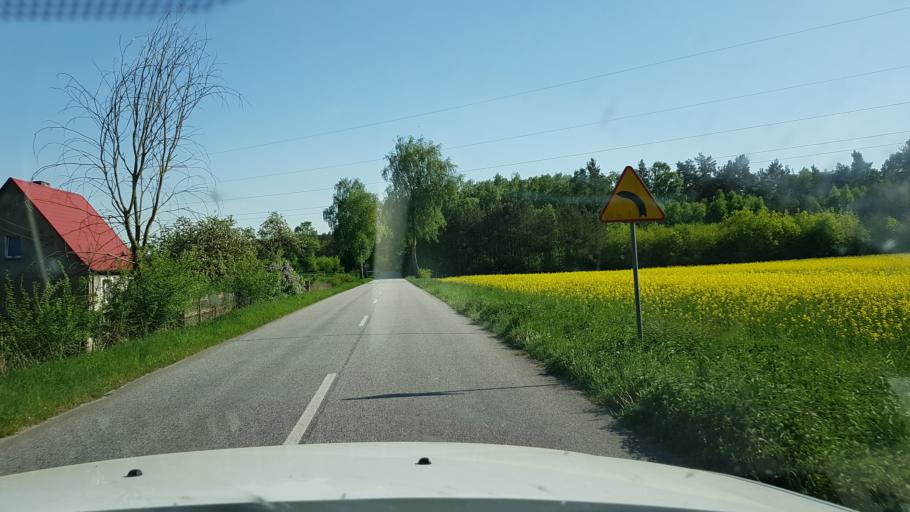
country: PL
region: West Pomeranian Voivodeship
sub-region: Powiat lobeski
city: Resko
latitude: 53.8197
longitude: 15.3959
